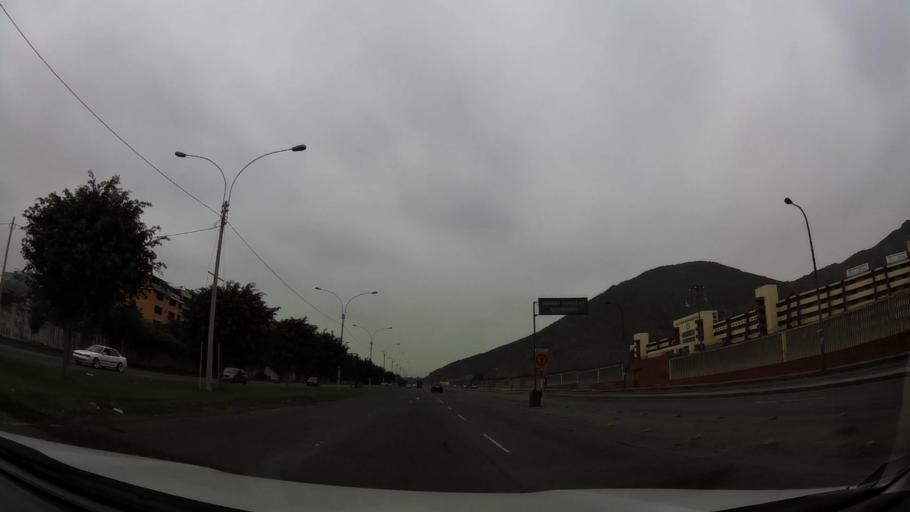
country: PE
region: Lima
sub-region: Lima
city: Vitarte
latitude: -12.0568
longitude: -76.9380
